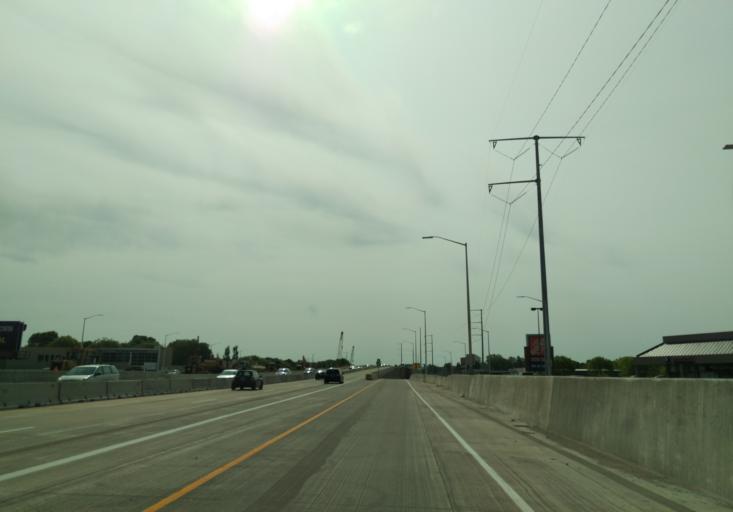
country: US
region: Wisconsin
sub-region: Dane County
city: Shorewood Hills
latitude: 43.0388
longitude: -89.4576
